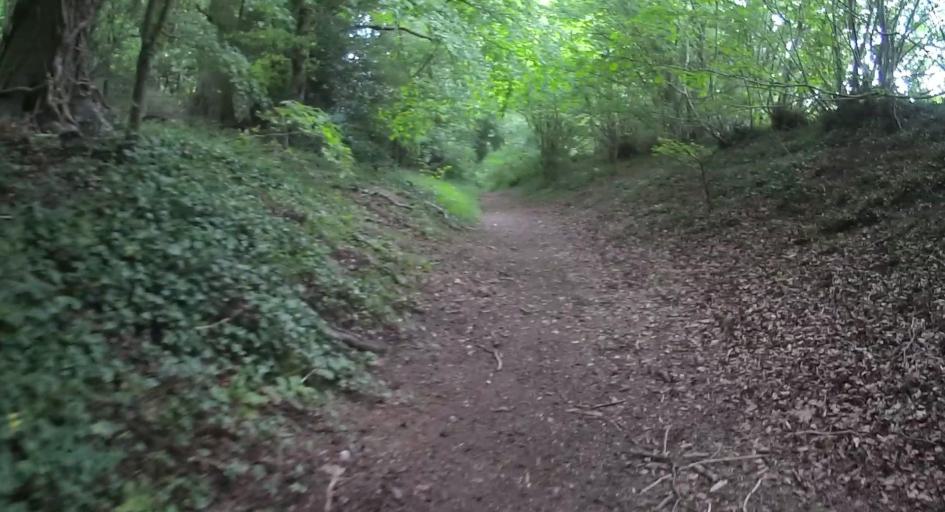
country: GB
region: England
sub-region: Hampshire
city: Four Marks
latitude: 51.1617
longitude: -1.1622
